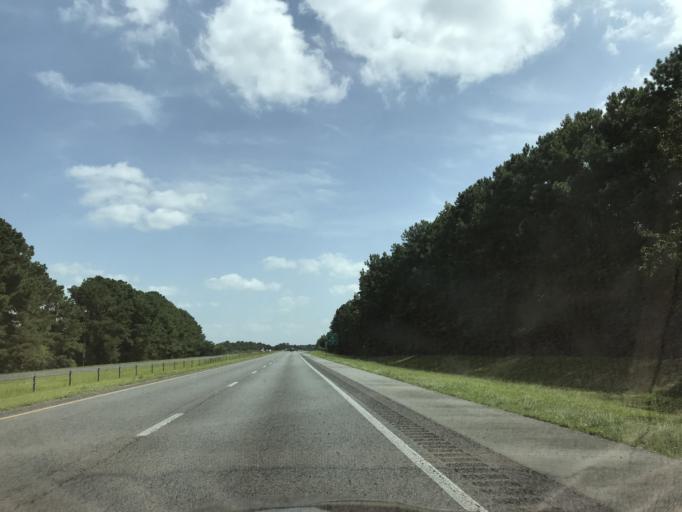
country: US
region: North Carolina
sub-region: Duplin County
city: Wallace
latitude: 34.7594
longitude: -77.9551
